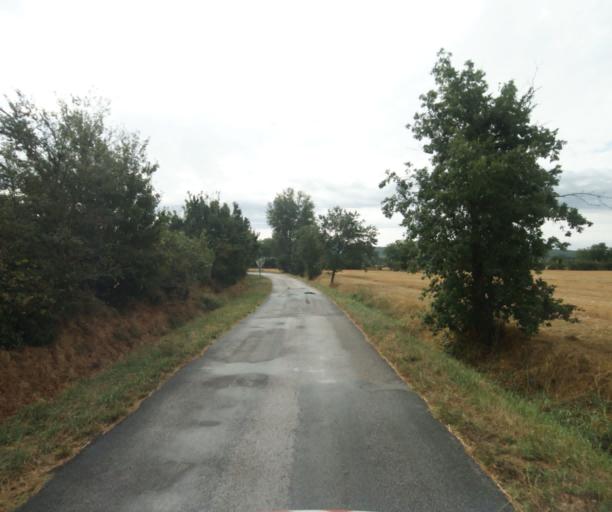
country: FR
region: Midi-Pyrenees
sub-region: Departement de la Haute-Garonne
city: Revel
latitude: 43.4259
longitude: 1.9554
